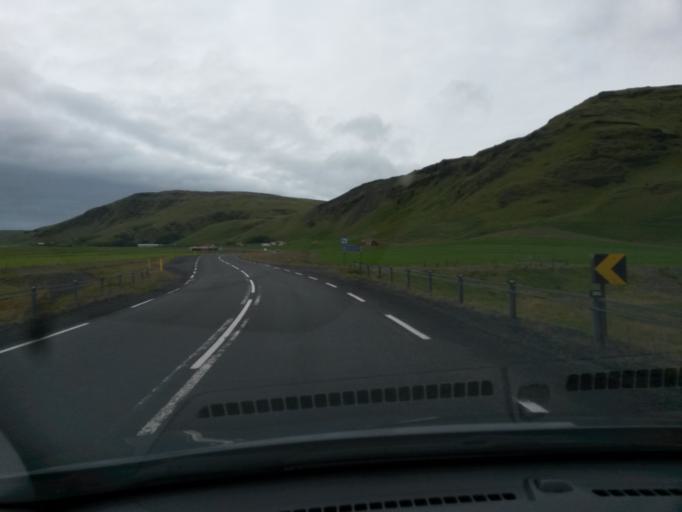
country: IS
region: South
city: Vestmannaeyjar
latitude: 63.4548
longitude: -19.0652
